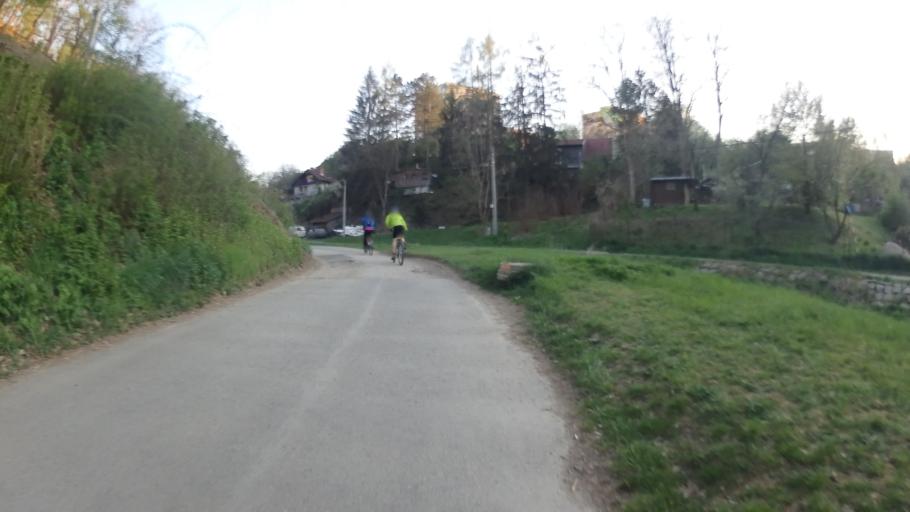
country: CZ
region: South Moravian
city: Troubsko
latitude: 49.2182
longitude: 16.5274
